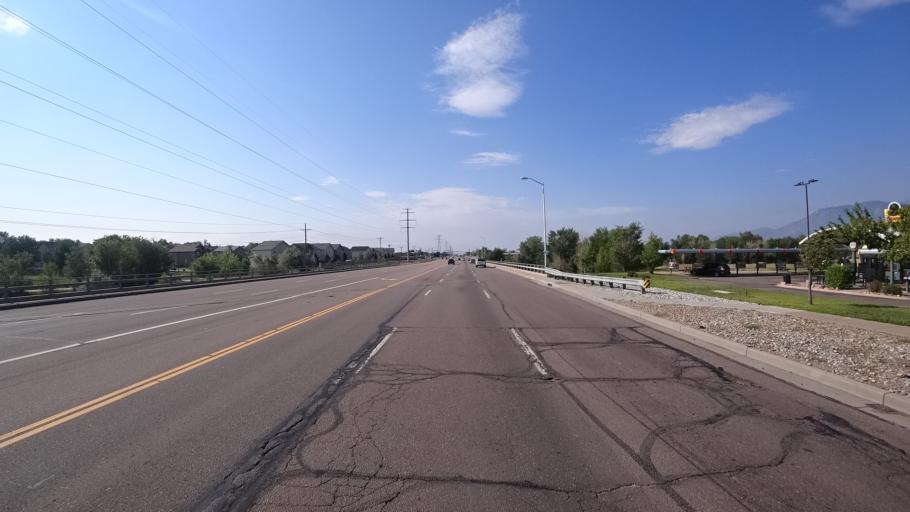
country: US
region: Colorado
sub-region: El Paso County
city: Stratmoor
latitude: 38.8008
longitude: -104.7577
